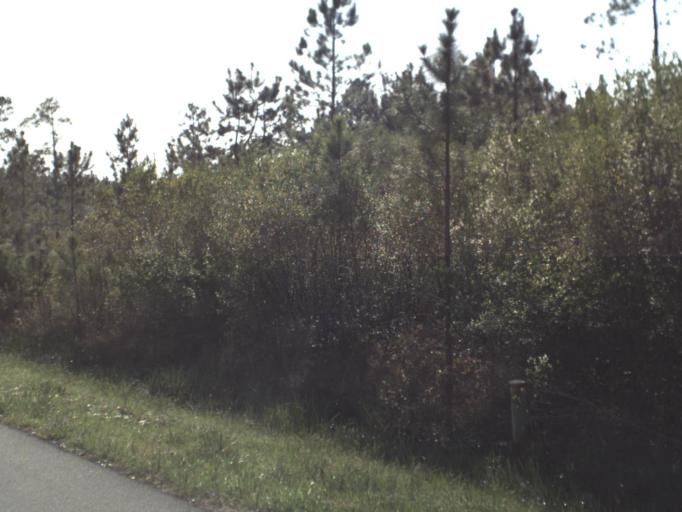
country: US
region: Florida
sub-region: Wakulla County
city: Crawfordville
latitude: 30.0275
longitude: -84.4986
